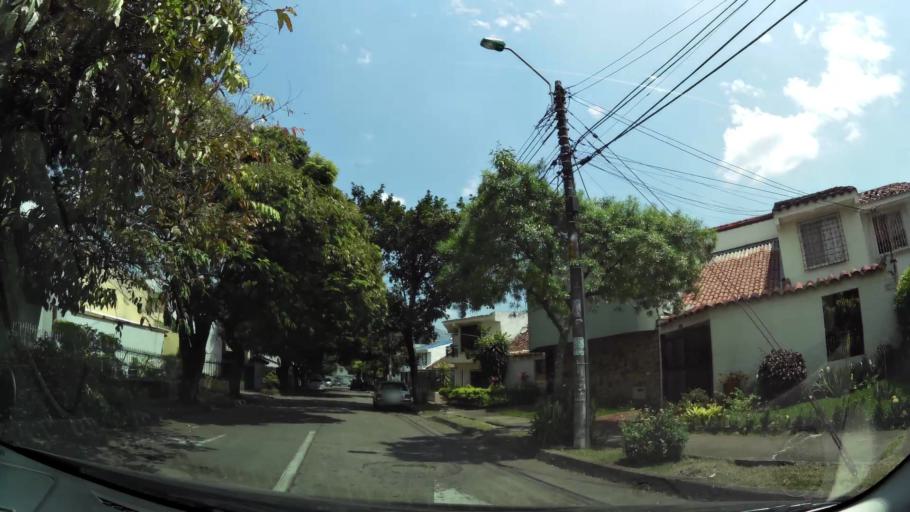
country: CO
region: Valle del Cauca
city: Cali
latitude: 3.4167
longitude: -76.5435
